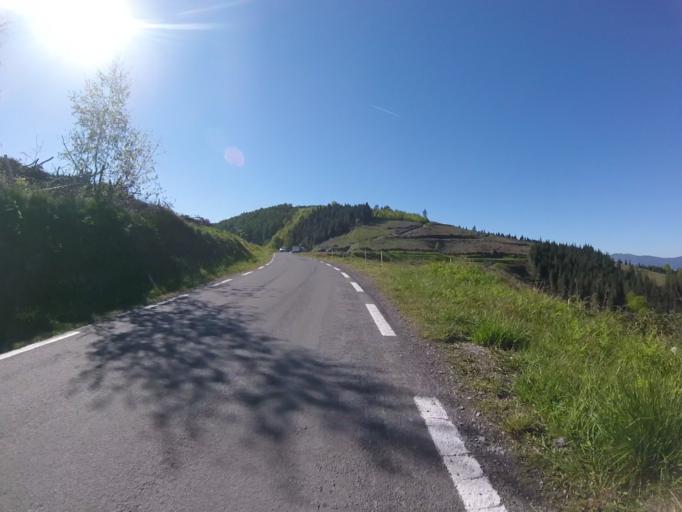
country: ES
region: Basque Country
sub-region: Provincia de Guipuzcoa
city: Errezil
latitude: 43.2036
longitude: -2.1980
